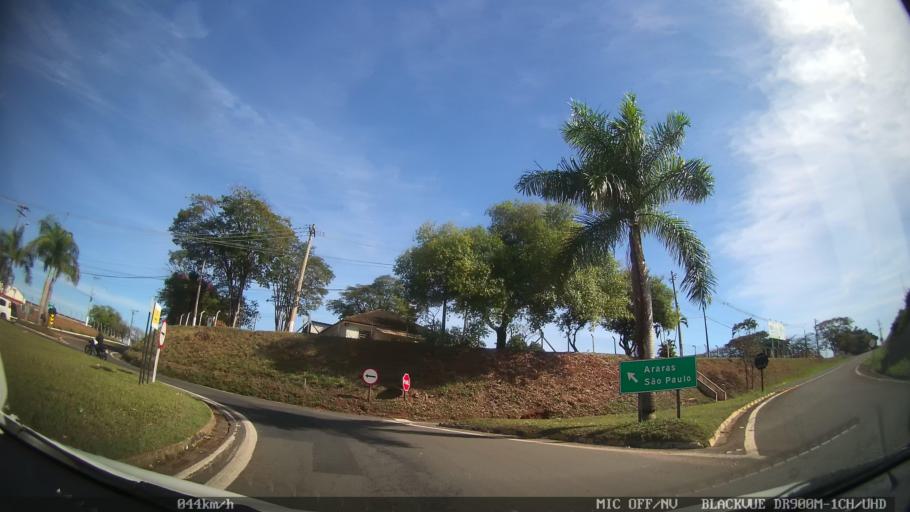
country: BR
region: Sao Paulo
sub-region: Leme
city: Leme
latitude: -22.2030
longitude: -47.3959
